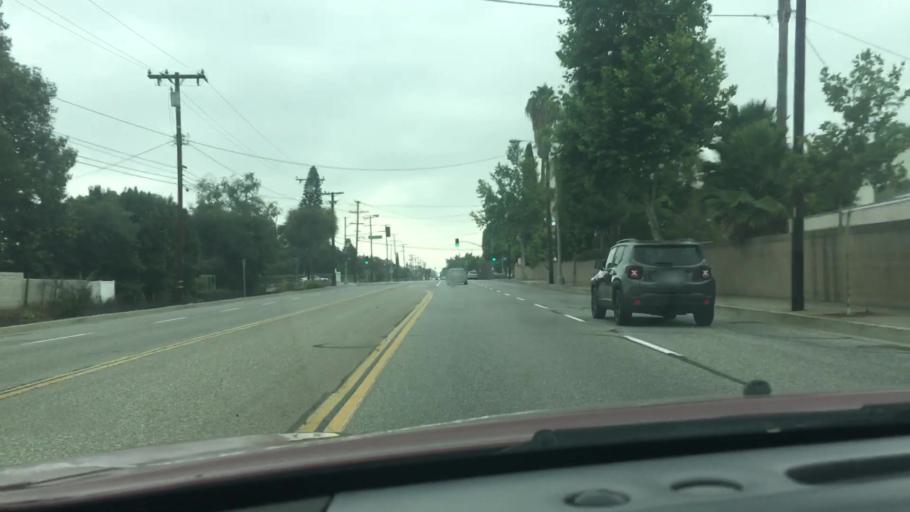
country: US
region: California
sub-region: Orange County
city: Fullerton
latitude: 33.8738
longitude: -117.9345
